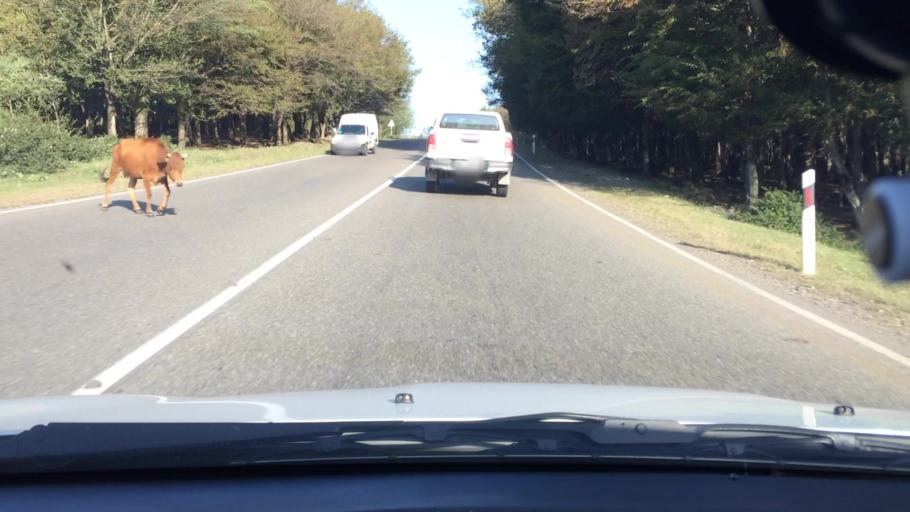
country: GE
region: Imereti
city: Kutaisi
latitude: 42.2284
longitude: 42.7800
